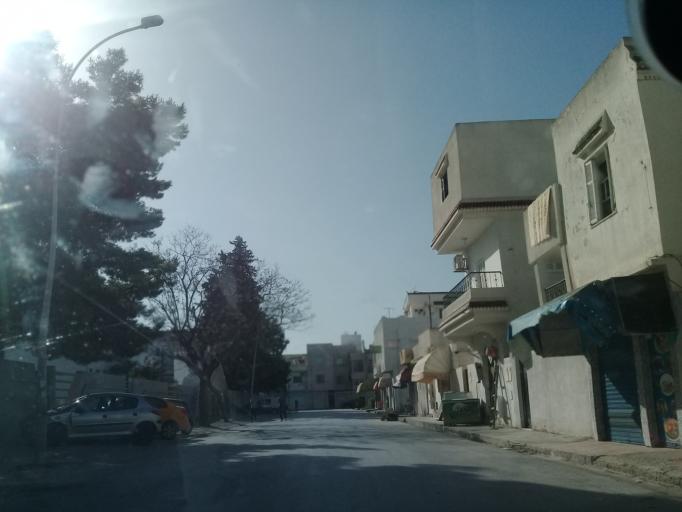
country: TN
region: Ariana
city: Ariana
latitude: 36.8331
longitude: 10.1918
